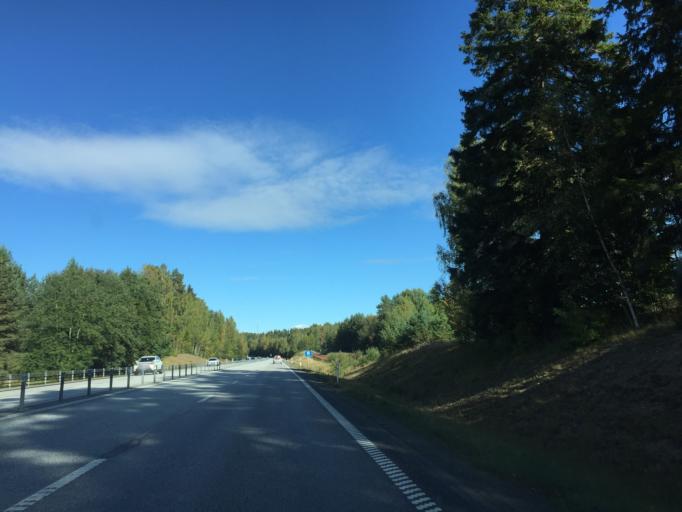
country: SE
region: OErebro
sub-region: Orebro Kommun
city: Hovsta
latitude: 59.3362
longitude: 15.2356
